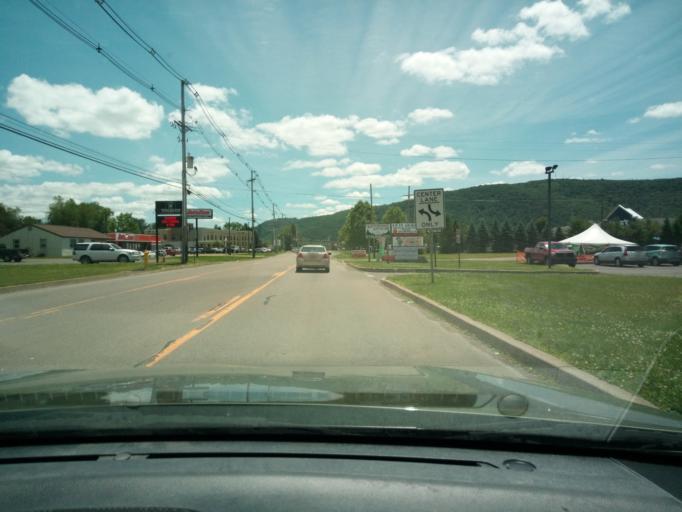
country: US
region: Pennsylvania
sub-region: Bradford County
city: South Waverly
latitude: 41.9818
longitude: -76.5431
